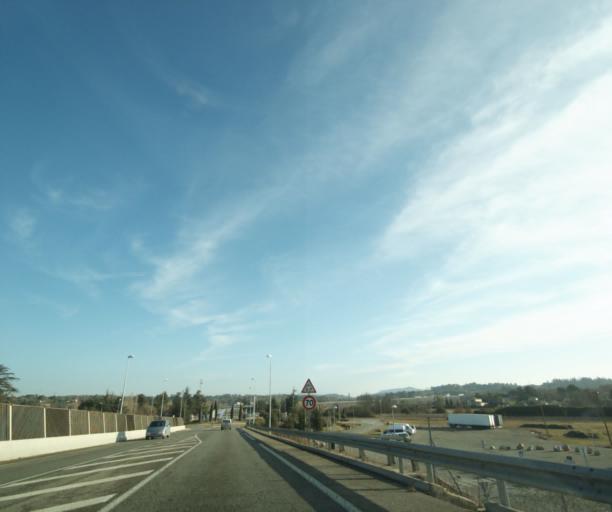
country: FR
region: Provence-Alpes-Cote d'Azur
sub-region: Departement du Var
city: Saint-Maximin-la-Sainte-Baume
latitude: 43.4476
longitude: 5.8743
